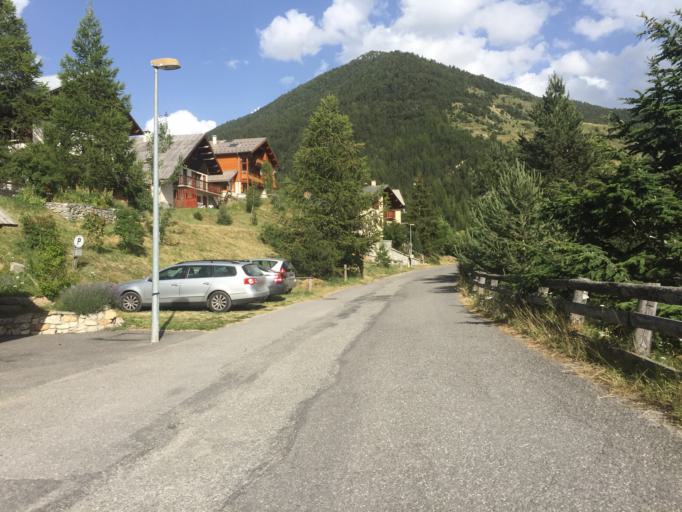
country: FR
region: Provence-Alpes-Cote d'Azur
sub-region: Departement des Hautes-Alpes
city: Guillestre
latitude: 44.6706
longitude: 6.7764
